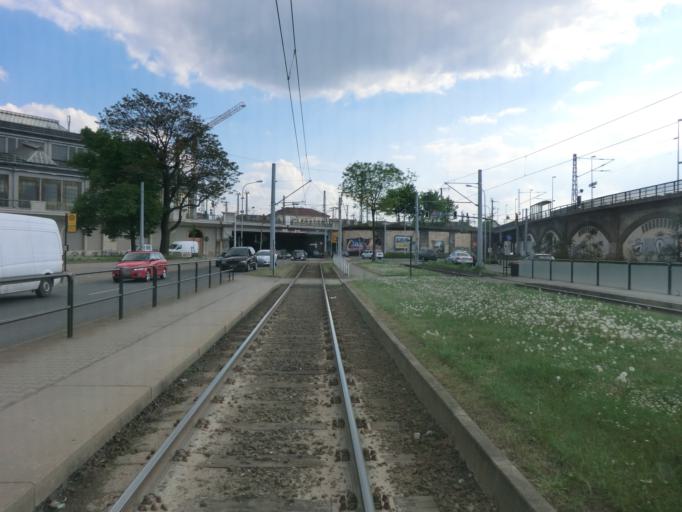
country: DE
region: Saxony
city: Dresden
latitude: 51.0663
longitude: 13.7395
